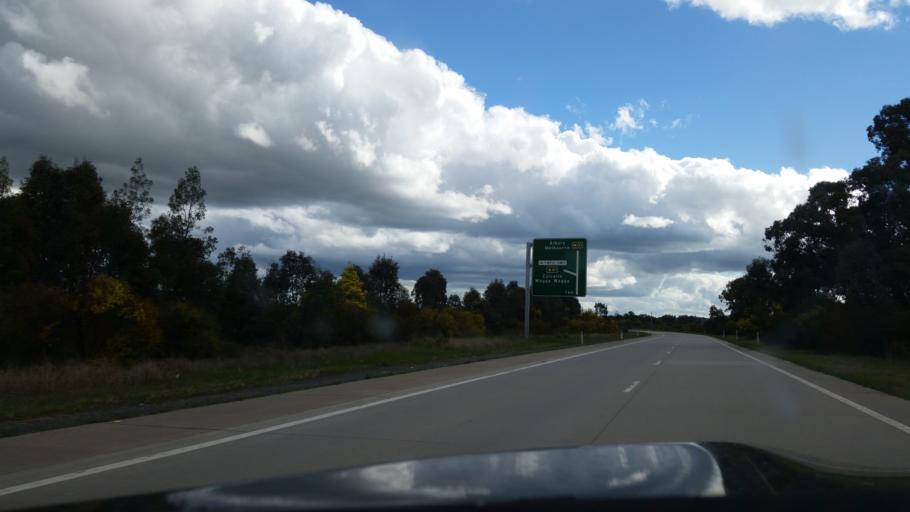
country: AU
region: New South Wales
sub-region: Greater Hume Shire
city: Jindera
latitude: -35.9249
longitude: 147.0157
